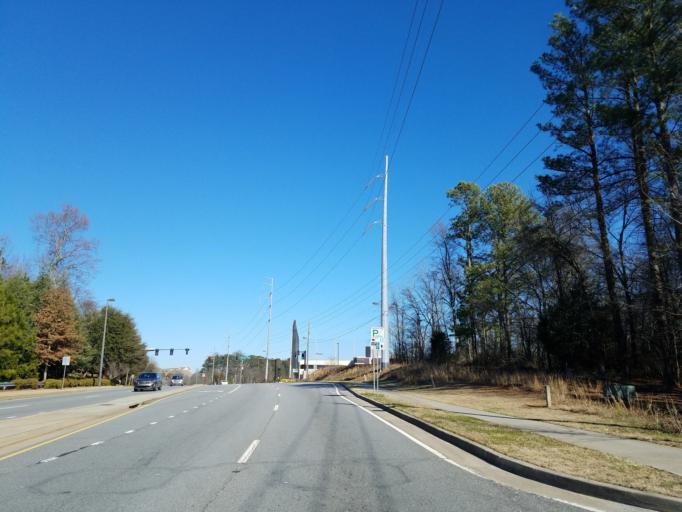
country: US
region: Georgia
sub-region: Fulton County
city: Alpharetta
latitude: 34.0442
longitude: -84.3108
